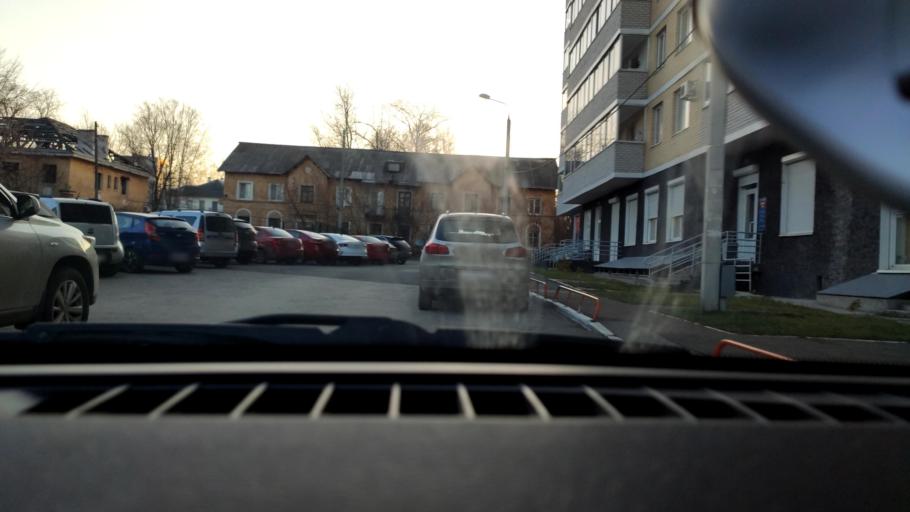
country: RU
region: Perm
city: Perm
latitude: 58.0010
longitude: 56.1831
